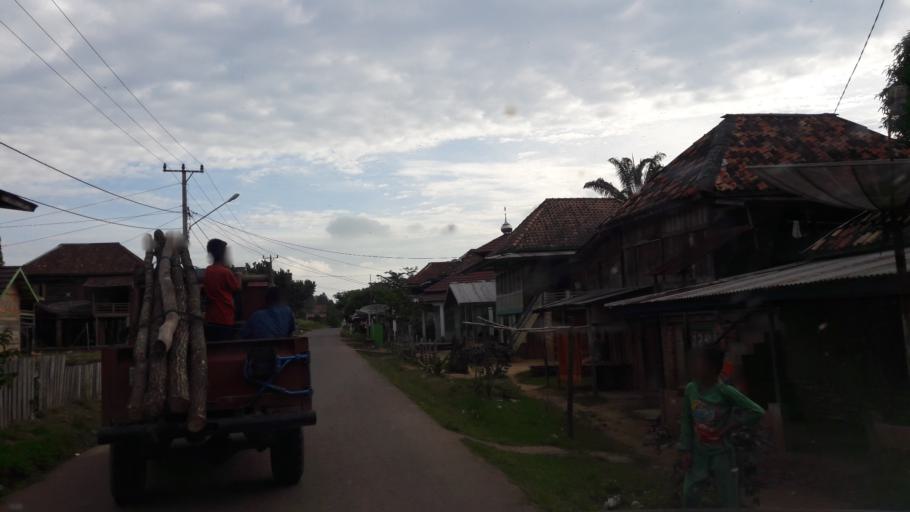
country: ID
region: South Sumatra
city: Gunungmenang
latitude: -3.2209
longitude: 103.8788
